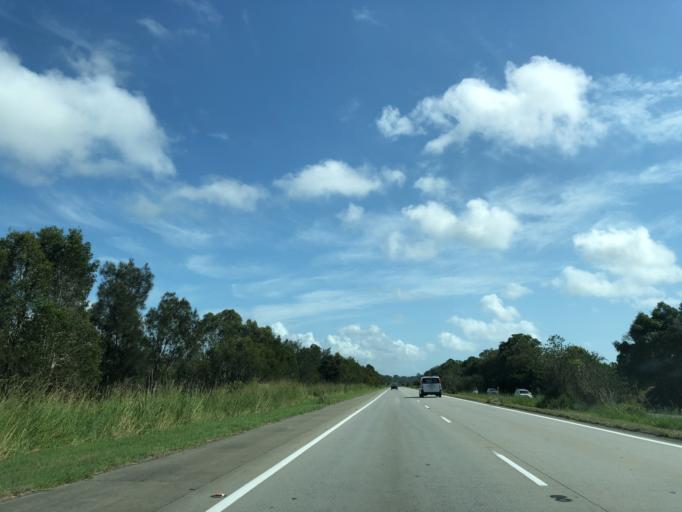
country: AU
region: New South Wales
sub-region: Byron Shire
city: Brunswick Heads
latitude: -28.5944
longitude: 153.5446
